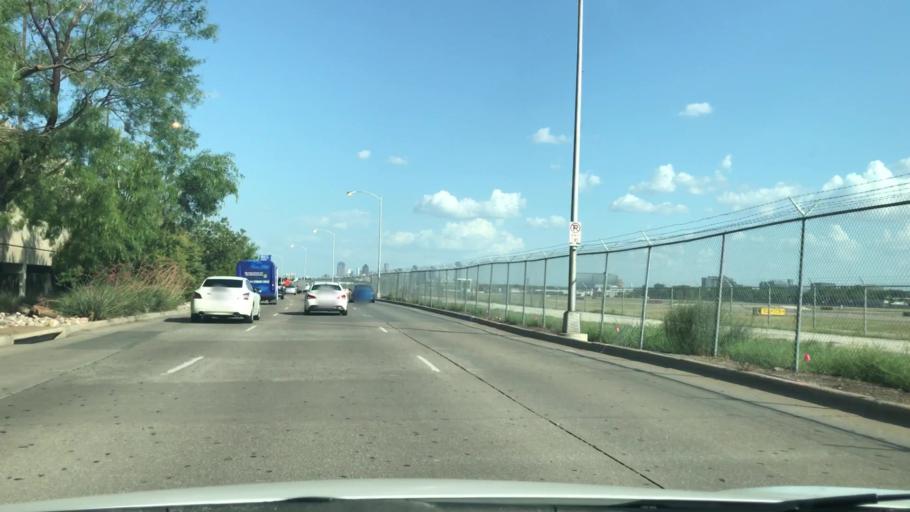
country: US
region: Texas
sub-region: Dallas County
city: University Park
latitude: 32.8425
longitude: -96.8504
